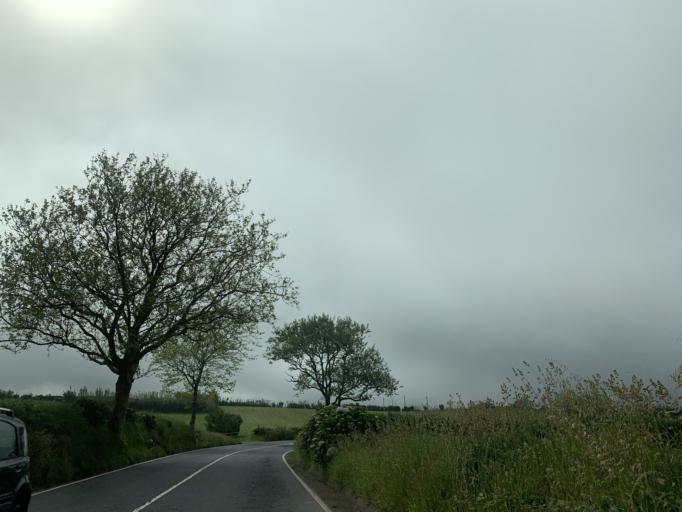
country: PT
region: Azores
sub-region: Ponta Delgada
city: Arrifes
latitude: 37.7729
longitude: -25.7420
